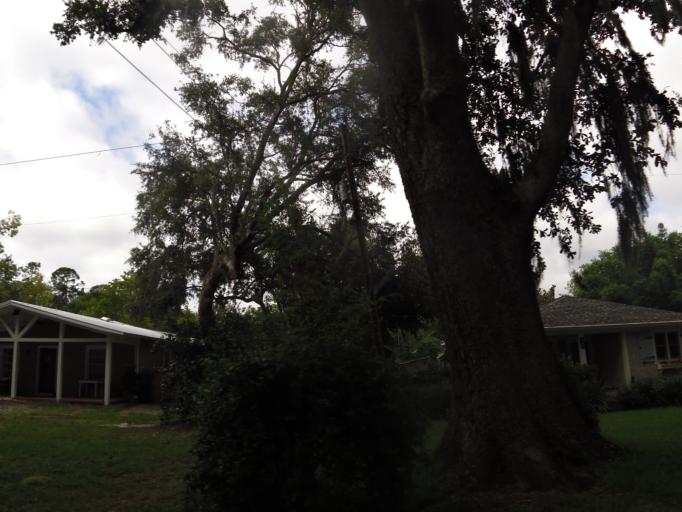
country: US
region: Georgia
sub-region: Glynn County
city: Saint Simons Island
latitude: 31.1382
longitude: -81.3927
